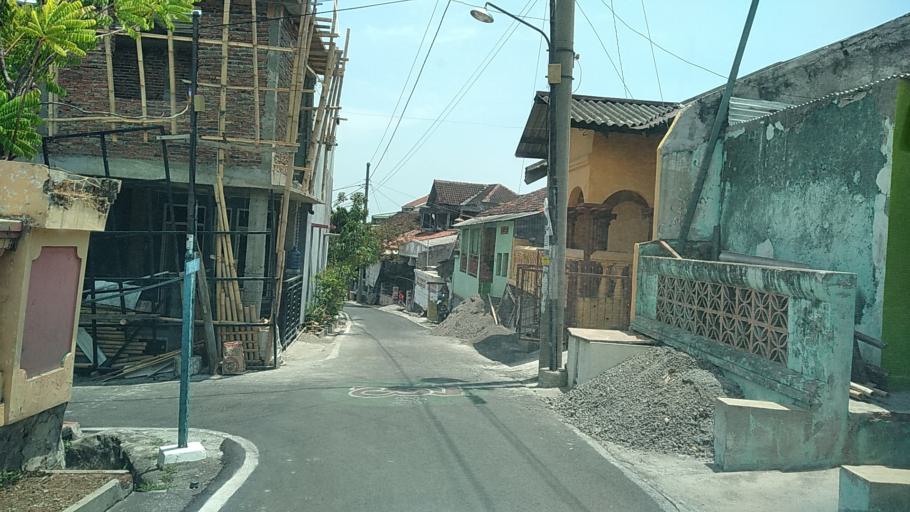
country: ID
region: Central Java
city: Semarang
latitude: -7.0123
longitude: 110.4486
